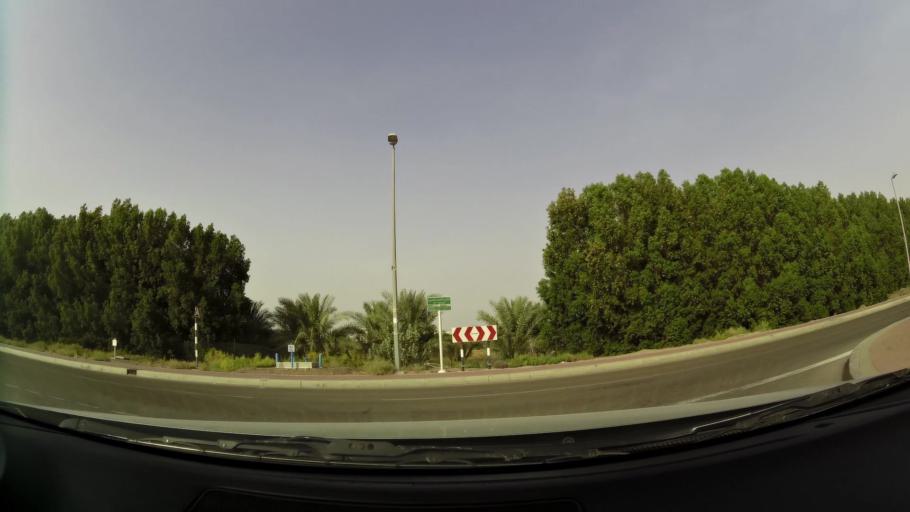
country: AE
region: Abu Dhabi
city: Al Ain
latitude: 24.2141
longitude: 55.6589
